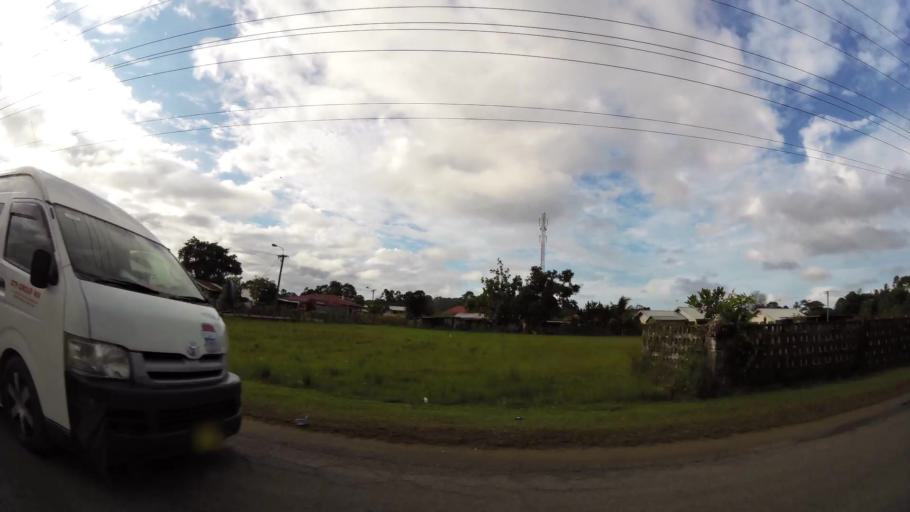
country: SR
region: Paramaribo
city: Paramaribo
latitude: 5.8480
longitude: -55.2480
